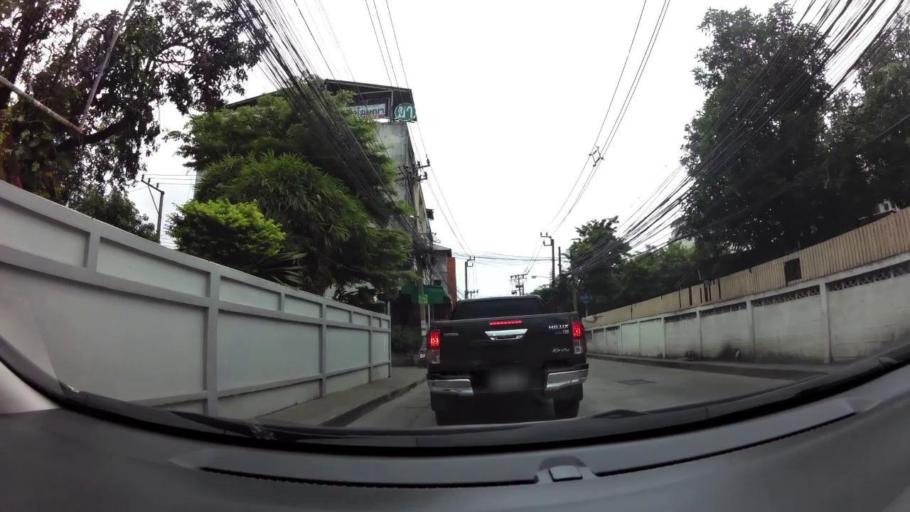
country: TH
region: Bangkok
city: Bang Na
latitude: 13.6787
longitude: 100.6374
